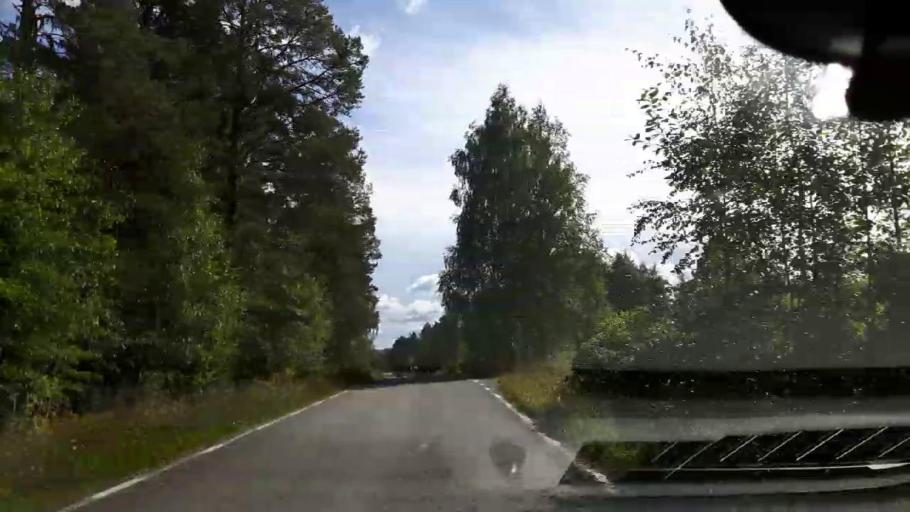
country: SE
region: Jaemtland
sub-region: Braecke Kommun
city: Braecke
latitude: 63.2136
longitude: 15.3430
